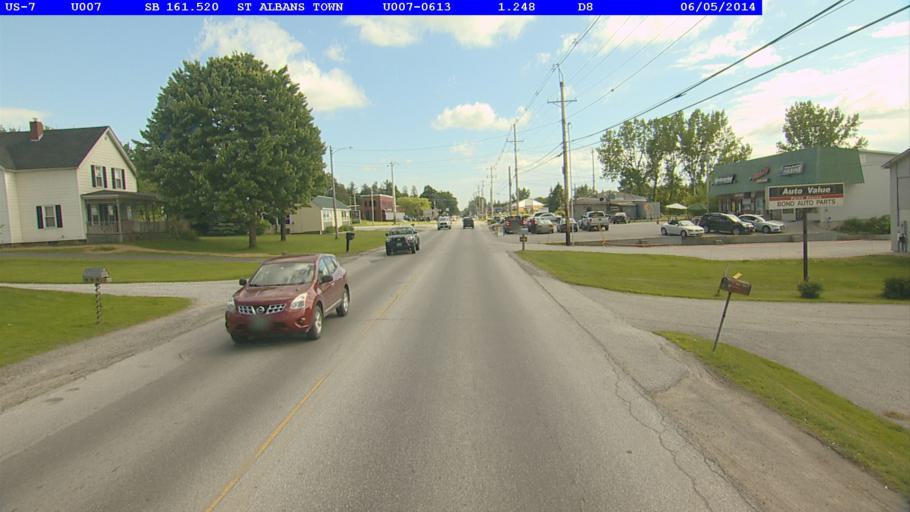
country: US
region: Vermont
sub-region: Franklin County
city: Saint Albans
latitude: 44.8267
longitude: -73.0804
